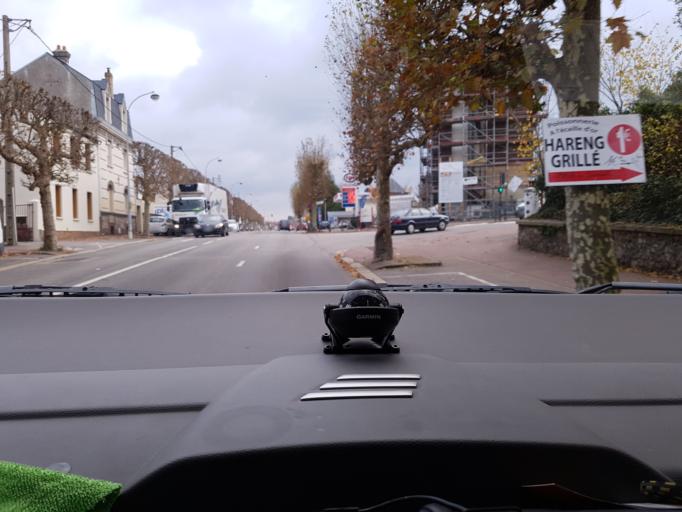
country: FR
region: Haute-Normandie
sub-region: Departement de la Seine-Maritime
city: Rouxmesnil-Bouteilles
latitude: 49.9169
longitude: 1.0743
